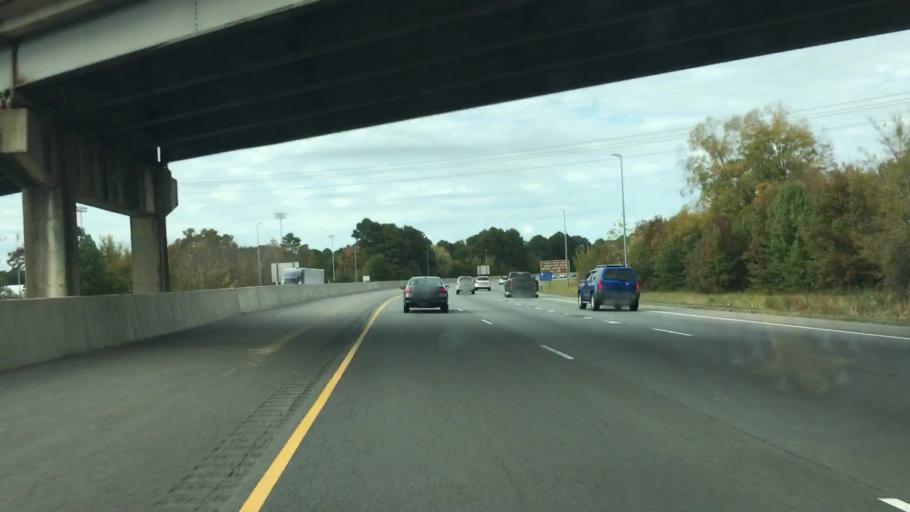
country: US
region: Arkansas
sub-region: Faulkner County
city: Conway
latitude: 35.0991
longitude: -92.4302
